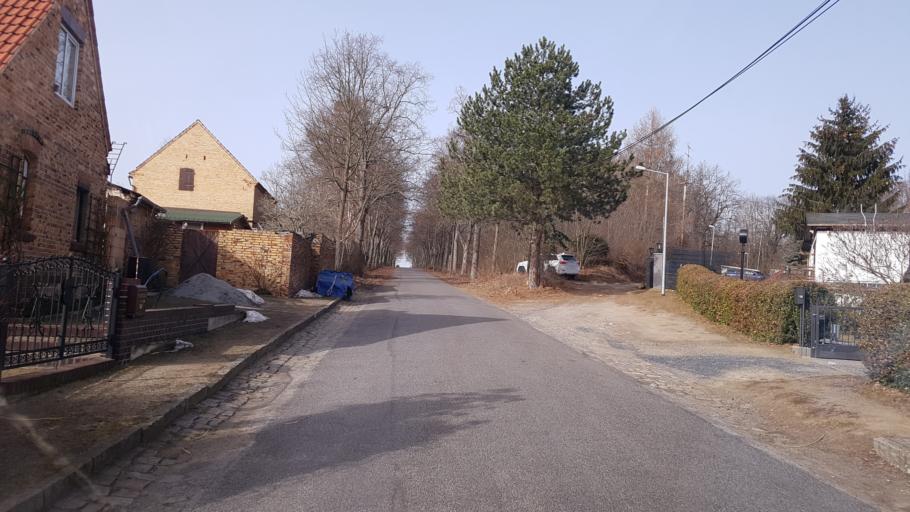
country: DE
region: Brandenburg
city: Schipkau
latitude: 51.5266
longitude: 13.8263
